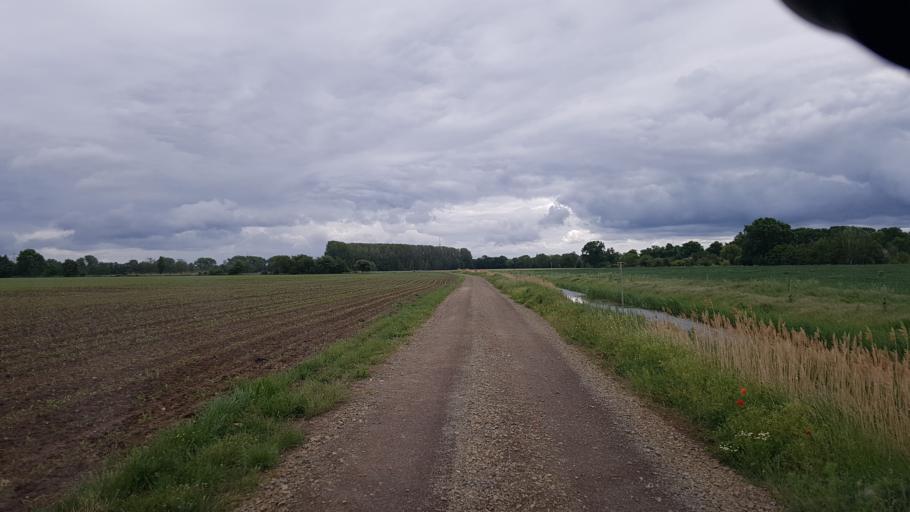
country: DE
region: Brandenburg
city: Doberlug-Kirchhain
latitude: 51.6554
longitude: 13.5479
